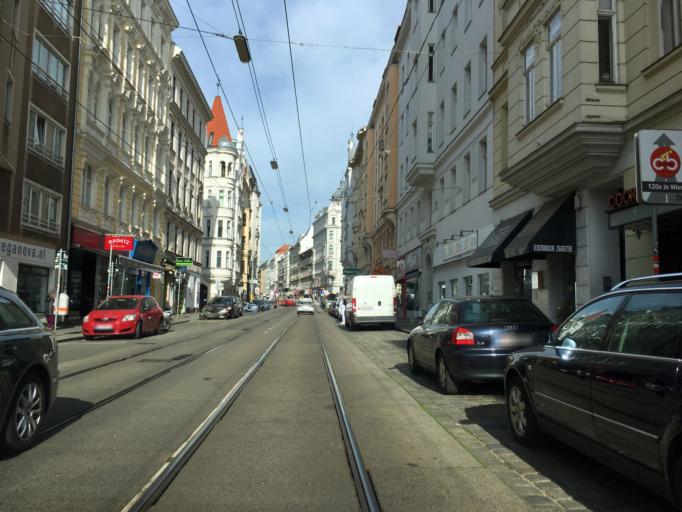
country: AT
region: Vienna
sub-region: Wien Stadt
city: Vienna
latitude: 48.2103
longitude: 16.3456
